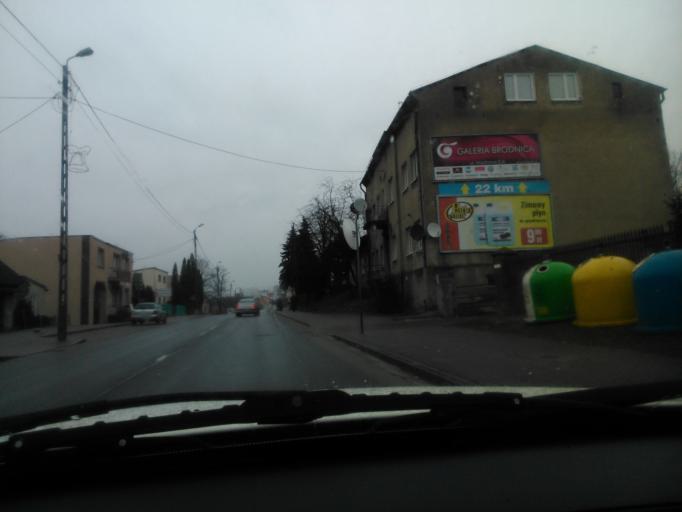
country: PL
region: Kujawsko-Pomorskie
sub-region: Powiat rypinski
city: Rypin
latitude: 53.0679
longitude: 19.4091
